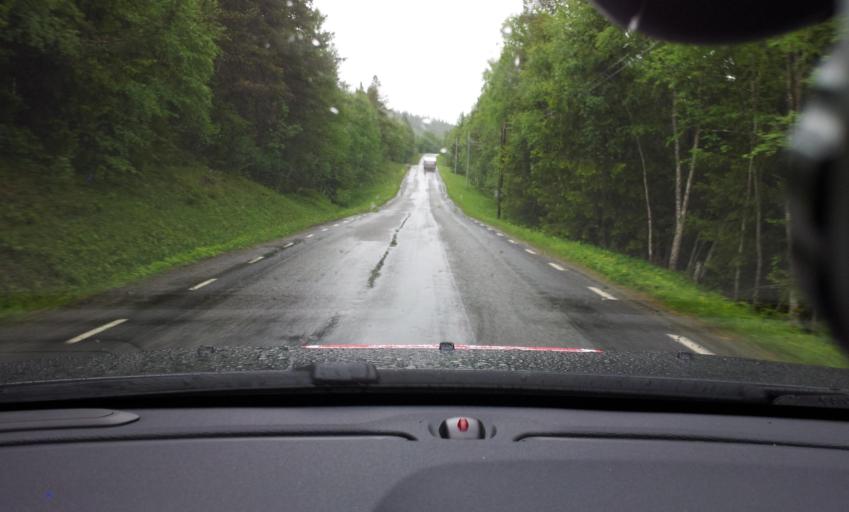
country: SE
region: Jaemtland
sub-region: Are Kommun
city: Are
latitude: 63.1489
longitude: 12.9962
